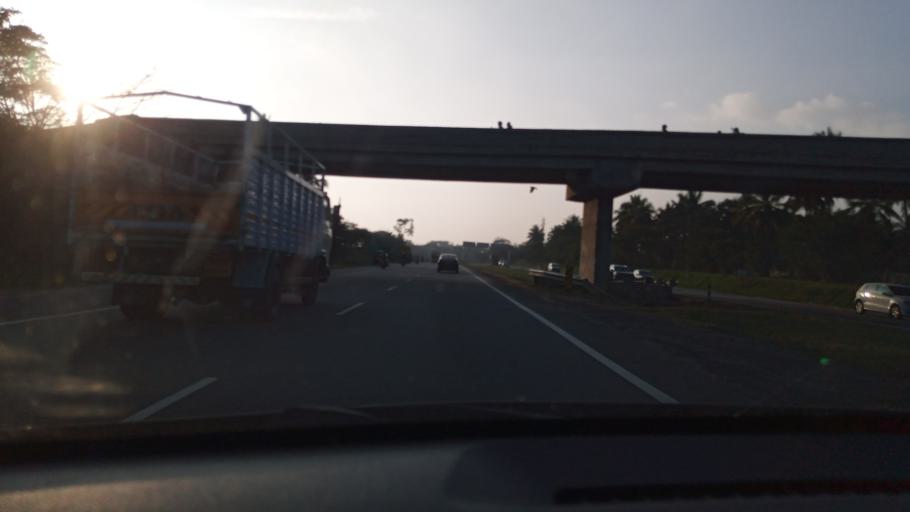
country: IN
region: Karnataka
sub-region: Bangalore Urban
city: Bangalore
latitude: 12.8496
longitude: 77.5831
